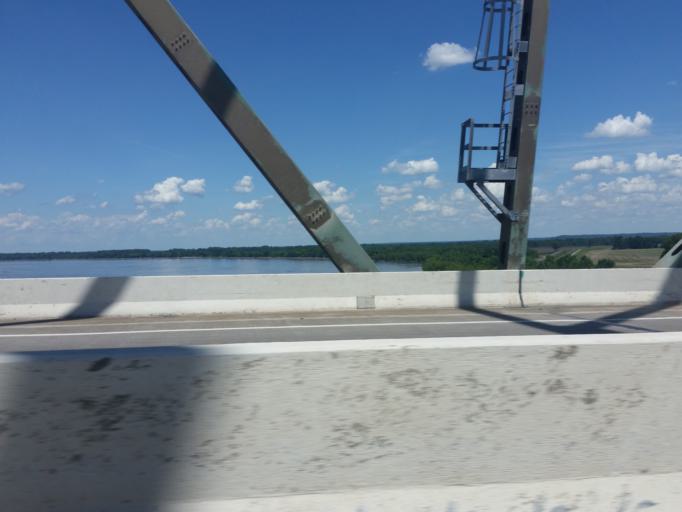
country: US
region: Missouri
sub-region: Pemiscot County
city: Caruthersville
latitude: 36.1125
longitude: -89.6116
